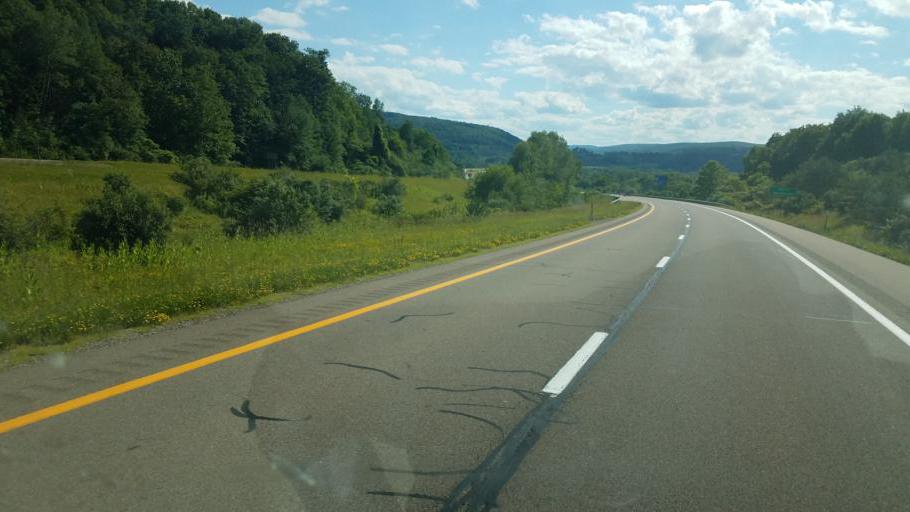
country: US
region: New York
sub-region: Steuben County
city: Hornell
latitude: 42.3792
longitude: -77.6661
